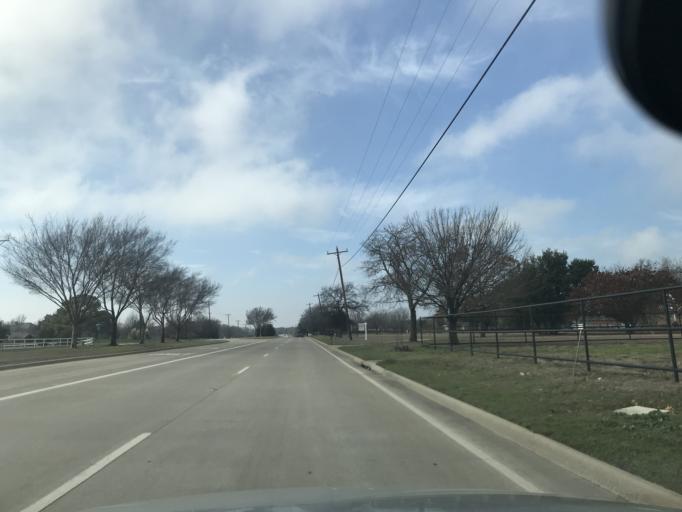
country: US
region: Texas
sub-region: Collin County
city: Parker
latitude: 33.0556
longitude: -96.6376
